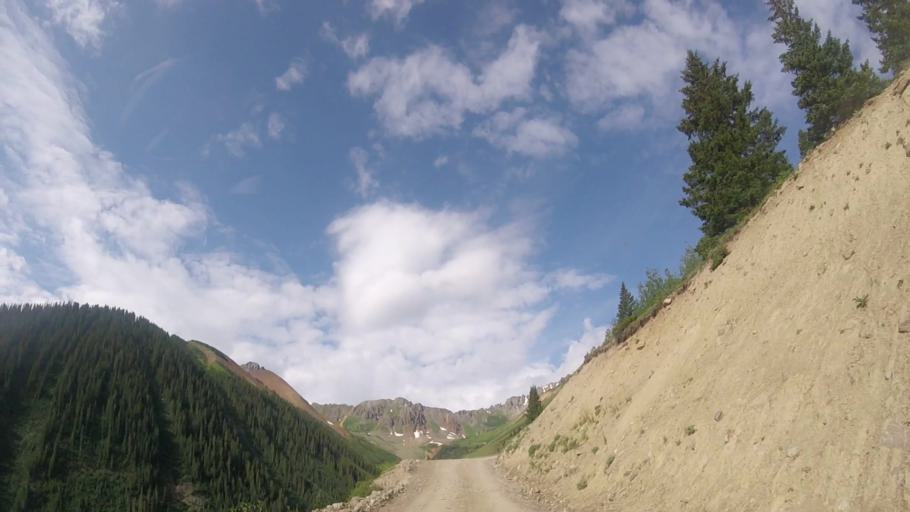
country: US
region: Colorado
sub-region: San Juan County
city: Silverton
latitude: 37.8465
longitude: -107.7608
